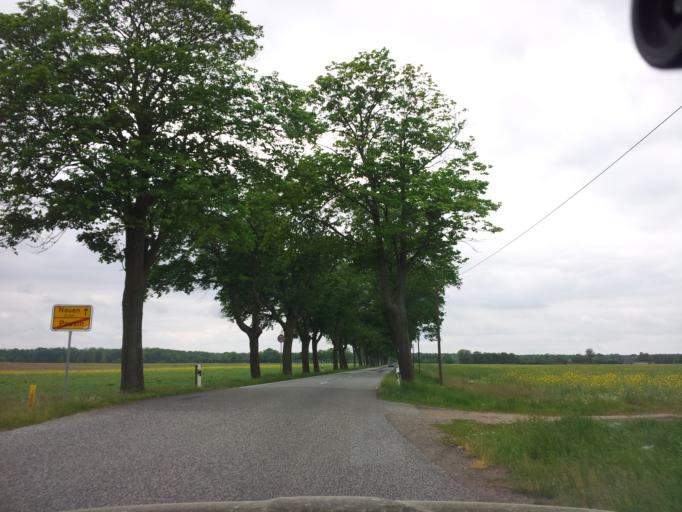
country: DE
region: Brandenburg
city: Brieselang
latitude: 52.6375
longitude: 13.0371
